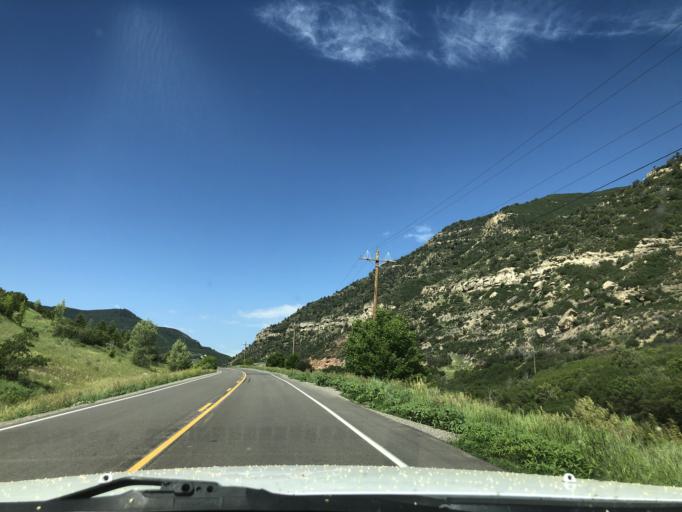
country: US
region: Colorado
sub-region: Delta County
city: Paonia
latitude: 38.9305
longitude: -107.4160
